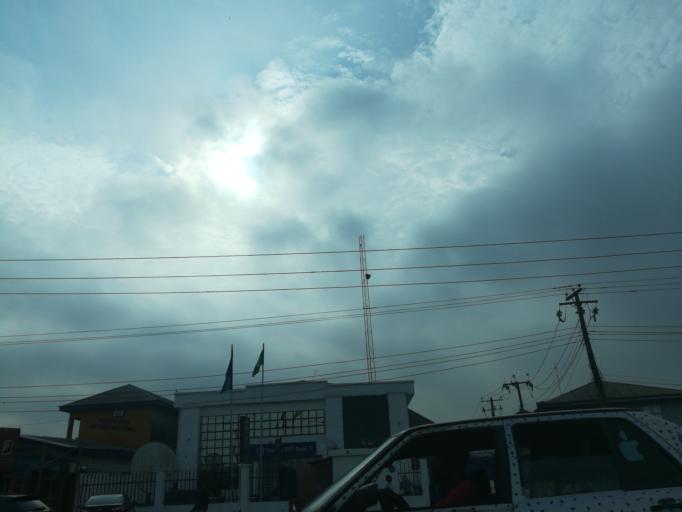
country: NG
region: Rivers
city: Port Harcourt
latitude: 4.8025
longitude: 6.9963
